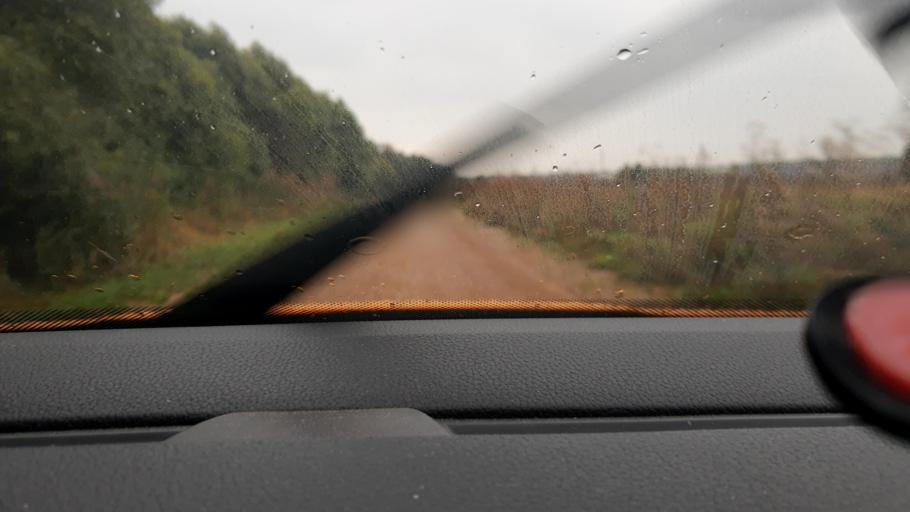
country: RU
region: Moskovskaya
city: Obukhovo
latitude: 55.8069
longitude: 38.2798
